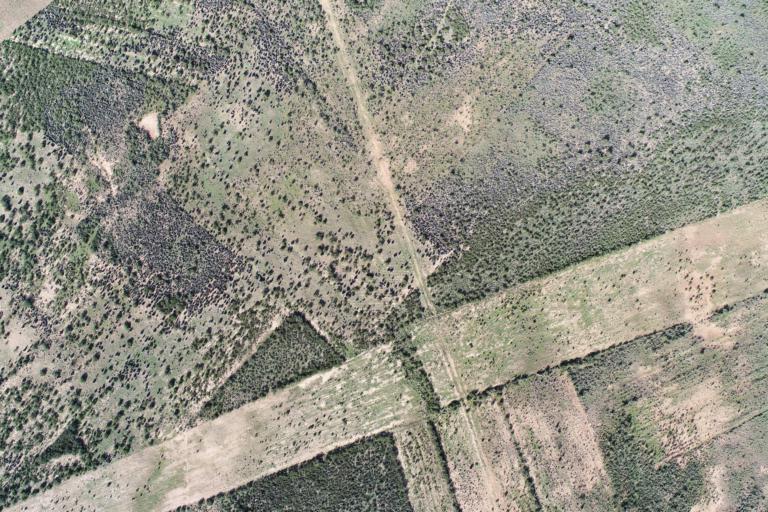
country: BO
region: La Paz
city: Curahuara de Carangas
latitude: -17.3006
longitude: -68.4985
